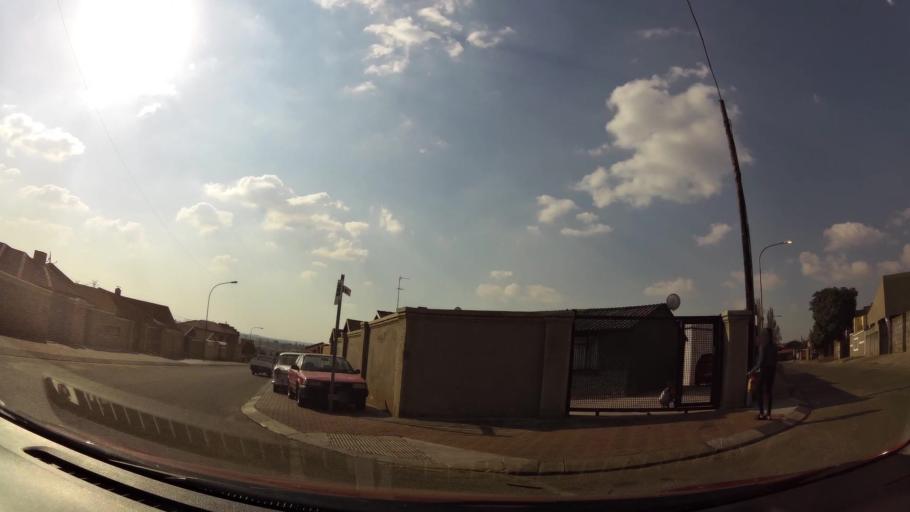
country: ZA
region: Gauteng
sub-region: City of Johannesburg Metropolitan Municipality
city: Soweto
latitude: -26.2368
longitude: 27.9432
